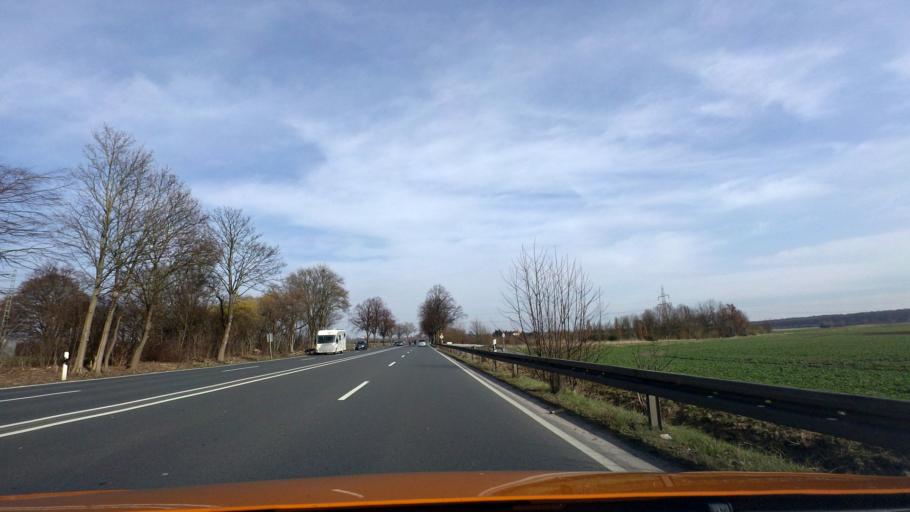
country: DE
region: Lower Saxony
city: Ronnenberg
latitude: 52.3201
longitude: 9.6691
